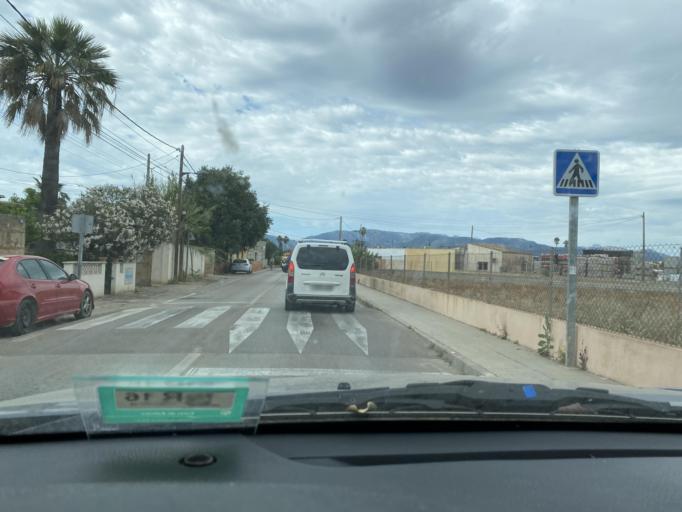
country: ES
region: Balearic Islands
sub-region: Illes Balears
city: Palma
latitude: 39.6086
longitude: 2.6797
